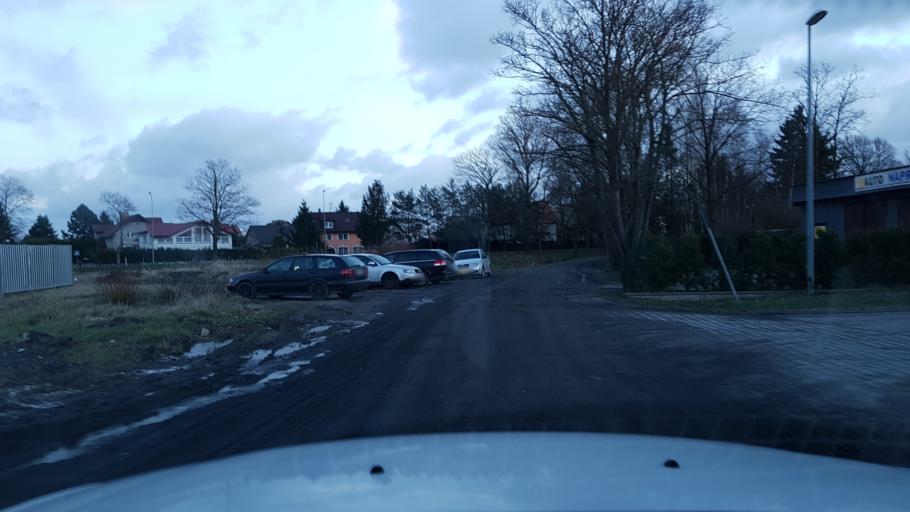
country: PL
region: West Pomeranian Voivodeship
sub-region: Powiat kolobrzeski
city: Kolobrzeg
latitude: 54.1501
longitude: 15.5592
